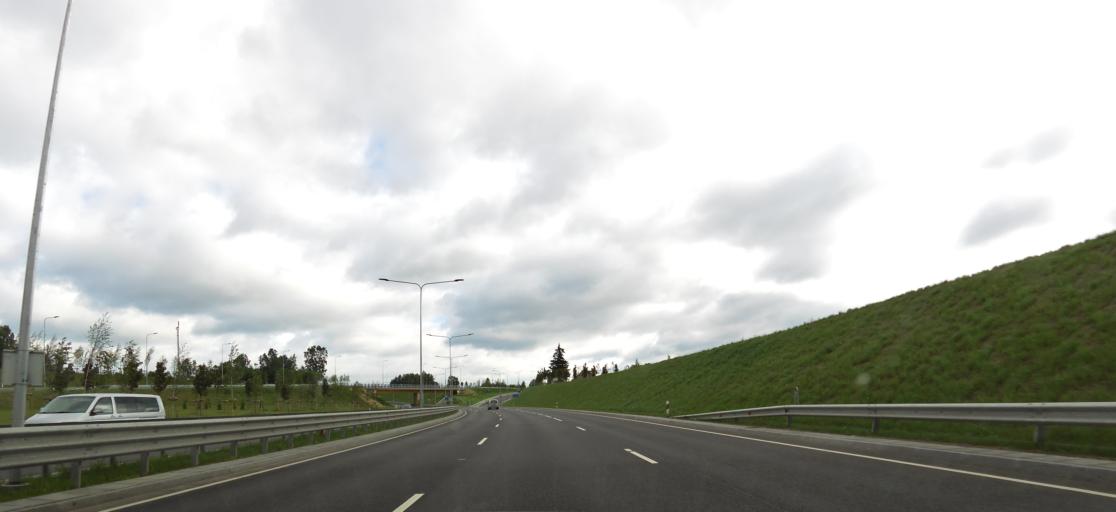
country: LT
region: Vilnius County
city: Pasilaiciai
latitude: 54.7422
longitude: 25.2174
